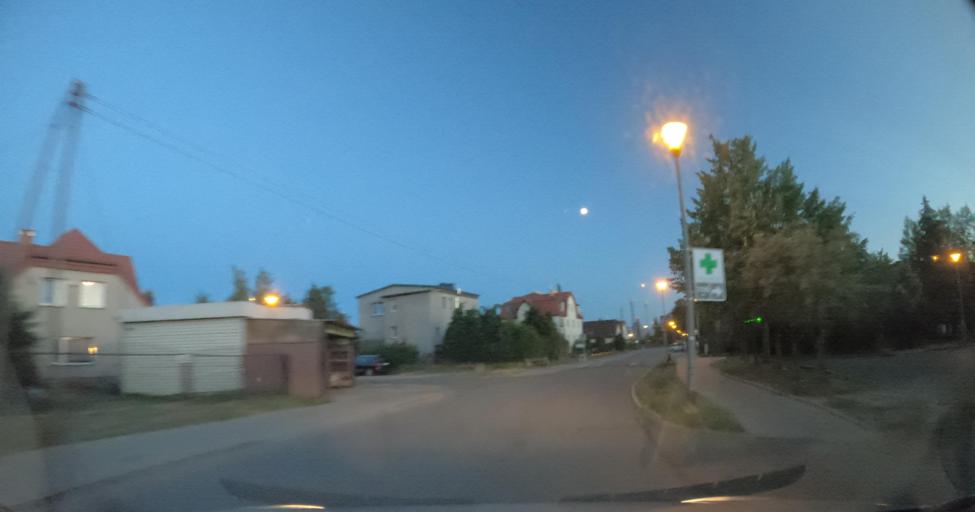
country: PL
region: Pomeranian Voivodeship
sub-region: Gdynia
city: Wielki Kack
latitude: 54.4306
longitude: 18.4705
